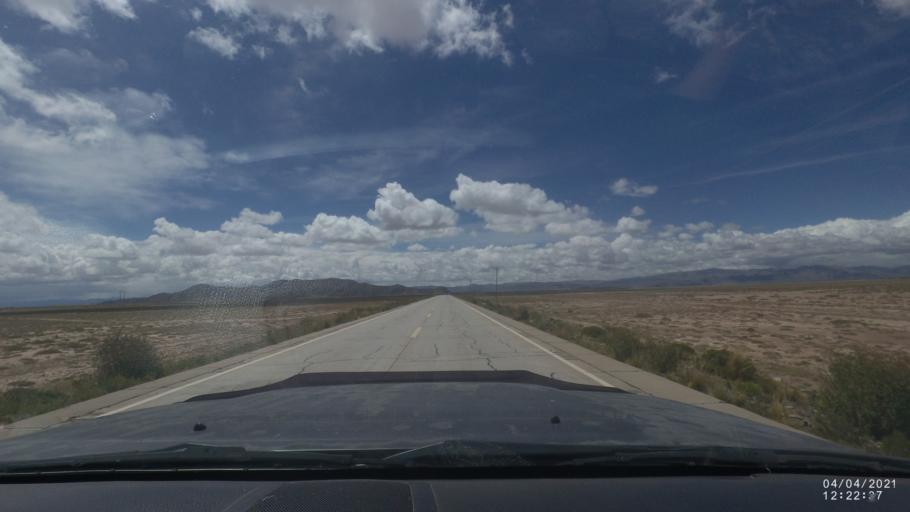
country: BO
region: Oruro
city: Oruro
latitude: -18.0566
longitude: -67.1965
